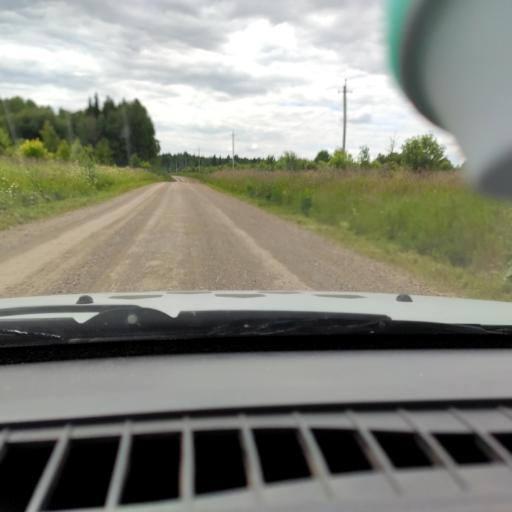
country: RU
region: Perm
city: Suksun
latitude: 57.2007
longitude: 57.6084
